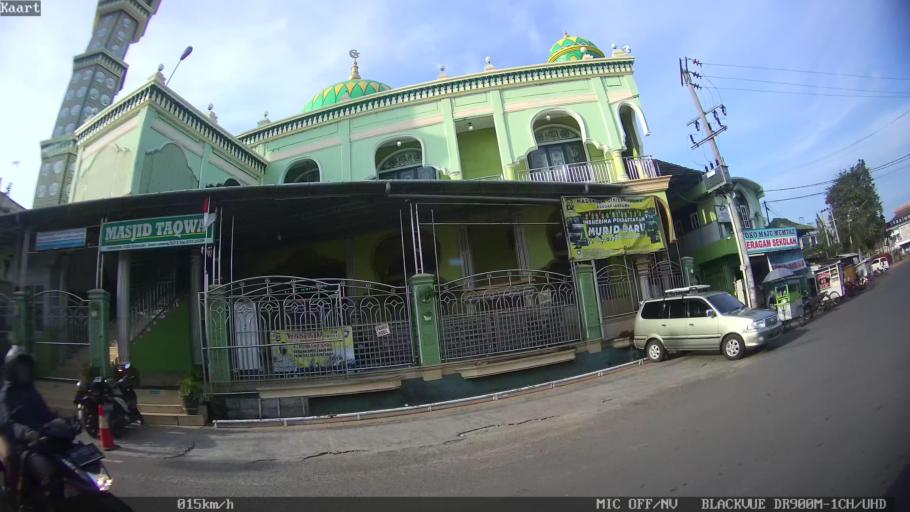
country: ID
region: Lampung
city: Bandarlampung
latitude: -5.4091
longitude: 105.2601
